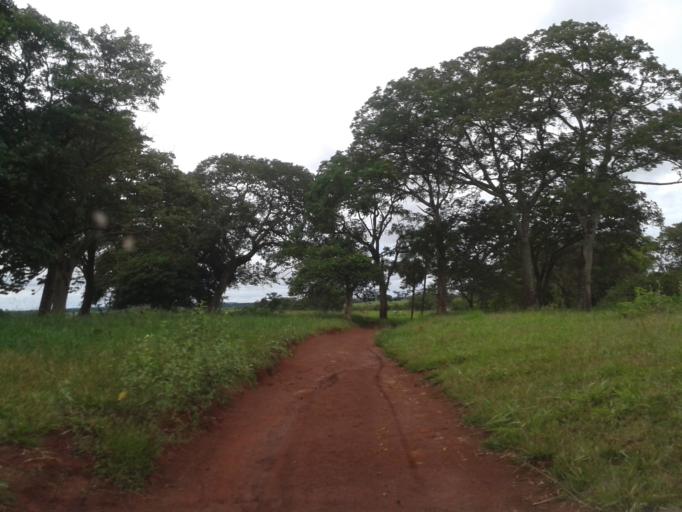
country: BR
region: Minas Gerais
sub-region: Capinopolis
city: Capinopolis
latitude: -18.7814
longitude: -49.7771
